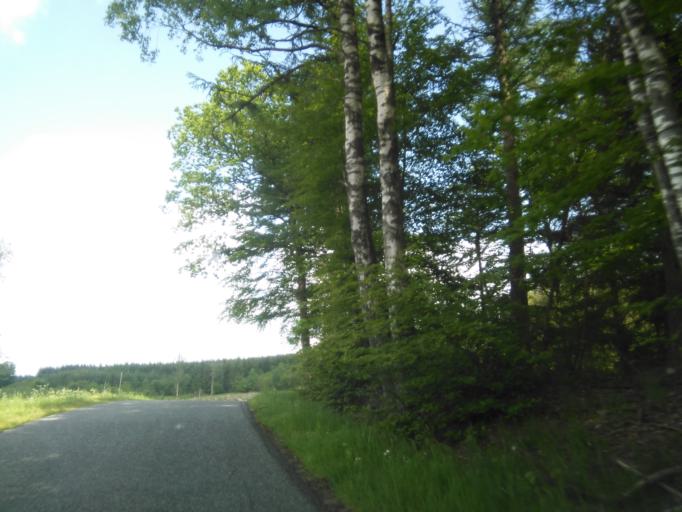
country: DK
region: Central Jutland
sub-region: Skanderborg Kommune
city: Galten
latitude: 56.2234
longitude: 9.9273
